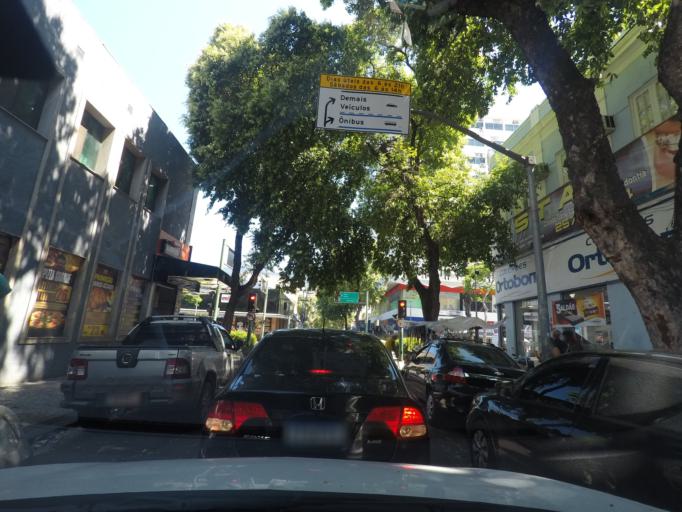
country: BR
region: Rio de Janeiro
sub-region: Rio De Janeiro
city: Rio de Janeiro
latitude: -22.9158
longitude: -43.2477
